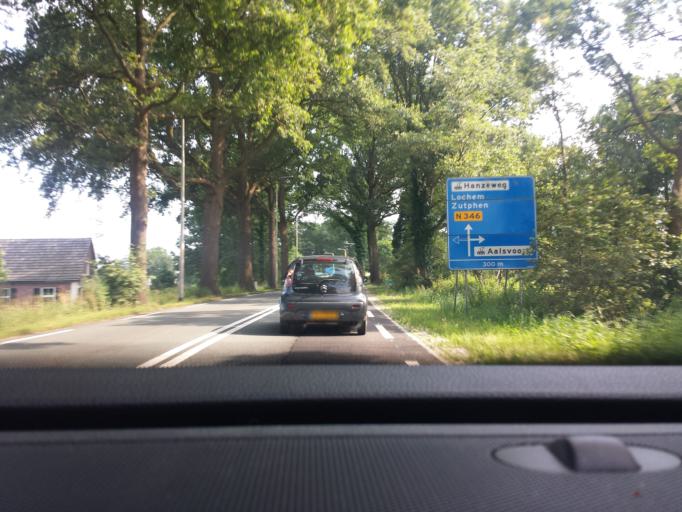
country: NL
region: Gelderland
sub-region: Gemeente Lochem
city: Lochem
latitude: 52.1716
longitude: 6.3918
